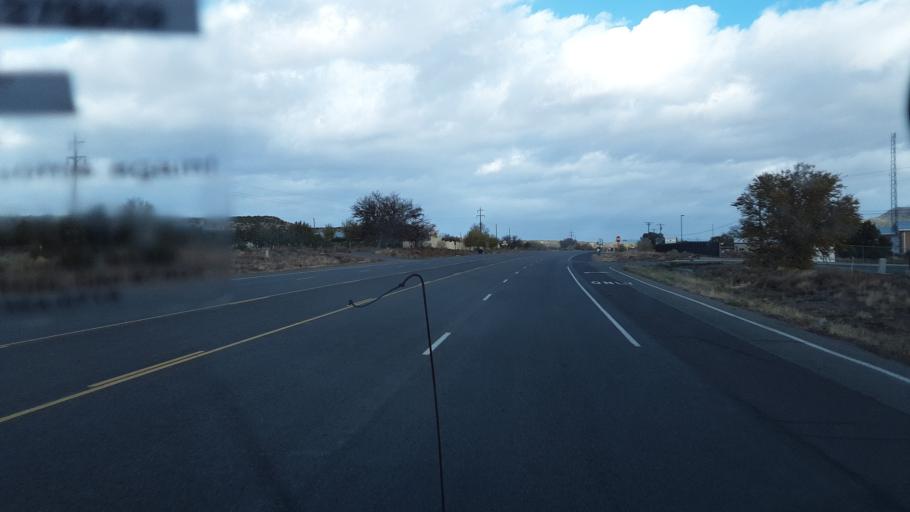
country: US
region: New Mexico
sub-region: Rio Arriba County
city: Ohkay Owingeh
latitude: 36.0512
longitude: -106.1132
